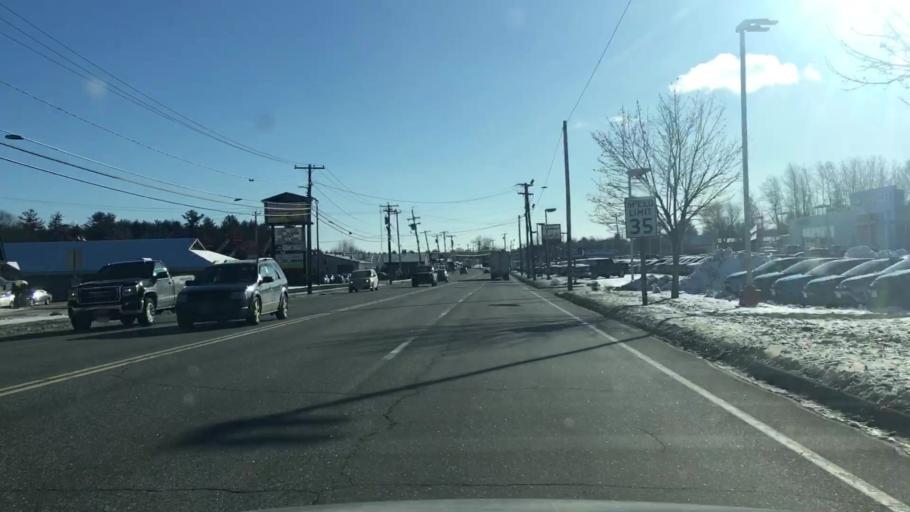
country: US
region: Maine
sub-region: Androscoggin County
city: Lewiston
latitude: 44.1351
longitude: -70.2257
